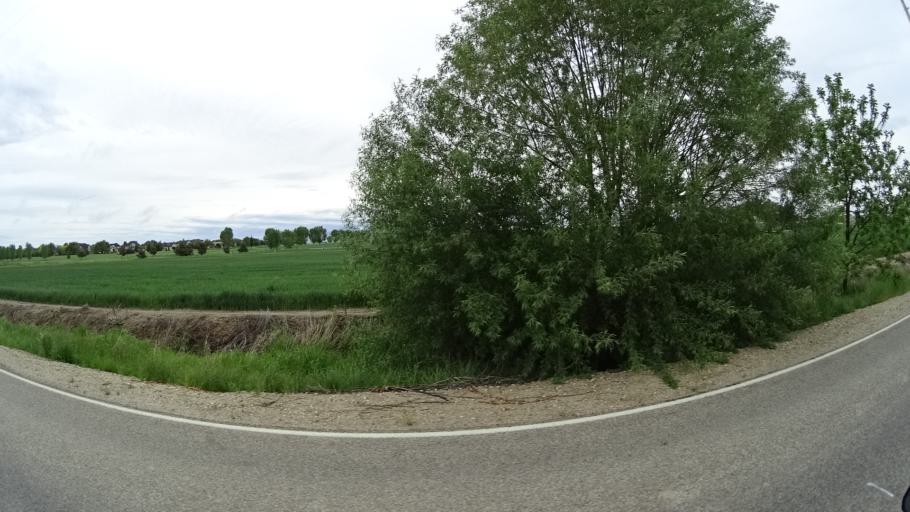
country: US
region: Idaho
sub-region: Ada County
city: Star
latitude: 43.7167
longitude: -116.4683
